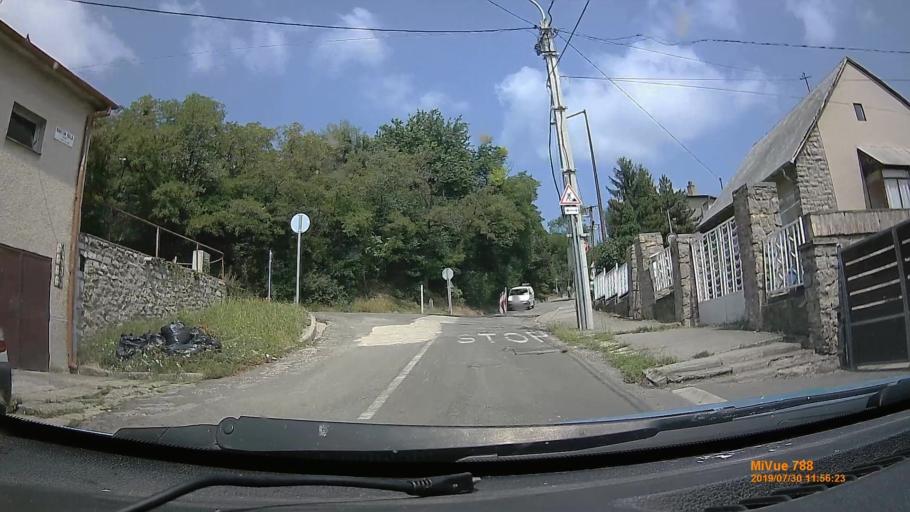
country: HU
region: Baranya
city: Pecs
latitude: 46.0832
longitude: 18.2186
